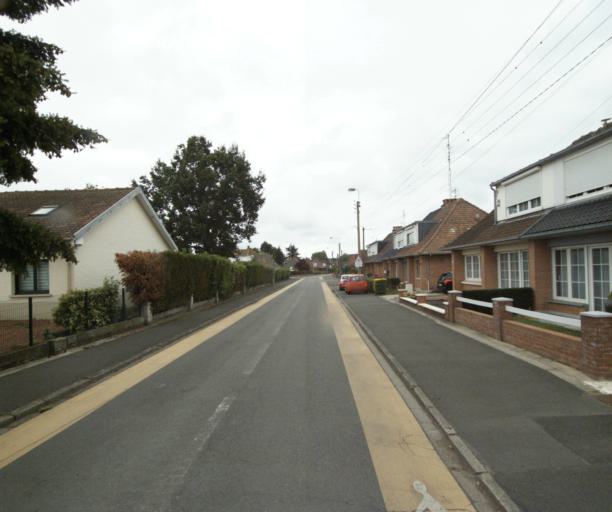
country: FR
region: Nord-Pas-de-Calais
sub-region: Departement du Nord
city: Leers
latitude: 50.6879
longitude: 3.2368
